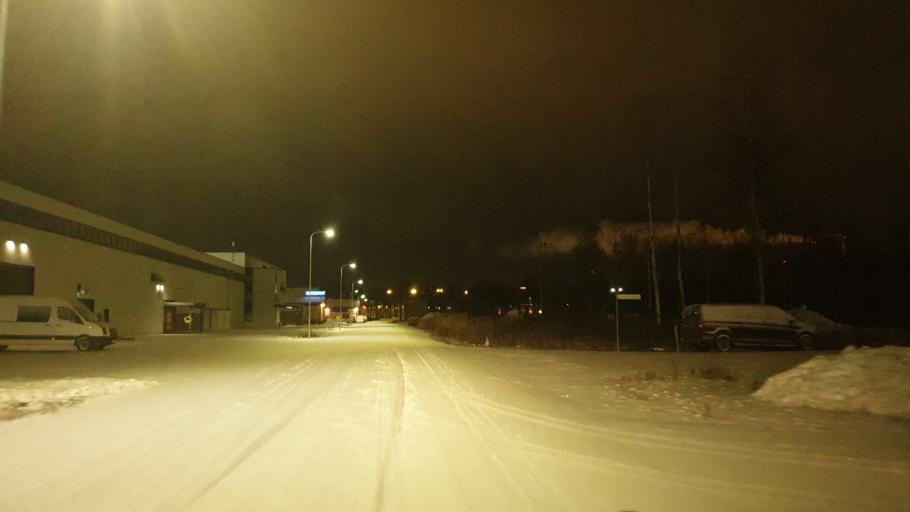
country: FI
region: Northern Ostrobothnia
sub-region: Oulu
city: Oulu
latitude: 64.9948
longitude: 25.4435
